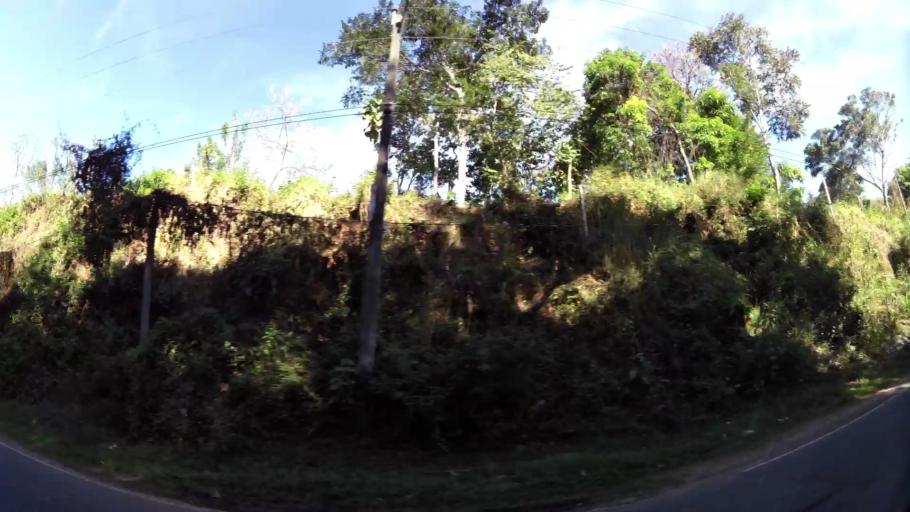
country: SV
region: Cuscatlan
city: Tenancingo
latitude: 13.8463
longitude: -89.0326
